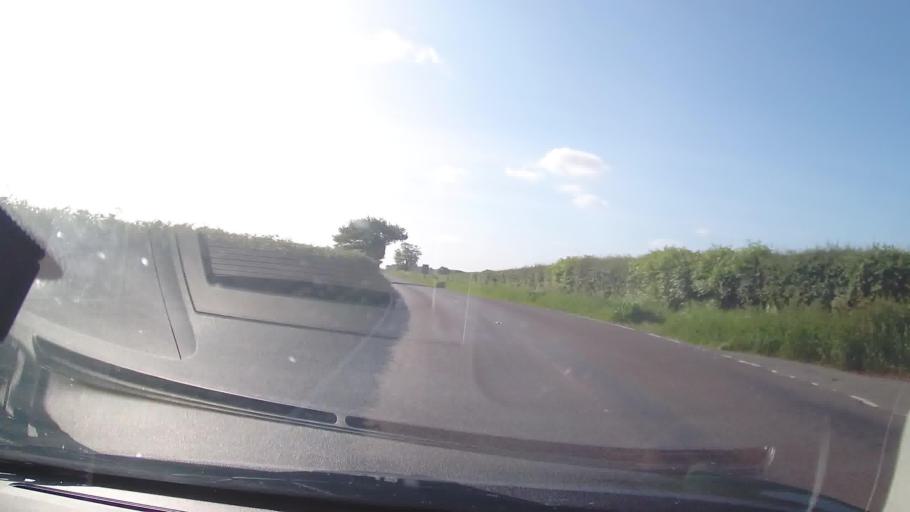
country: GB
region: England
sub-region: Shropshire
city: Shawbury
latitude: 52.7668
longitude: -2.6339
